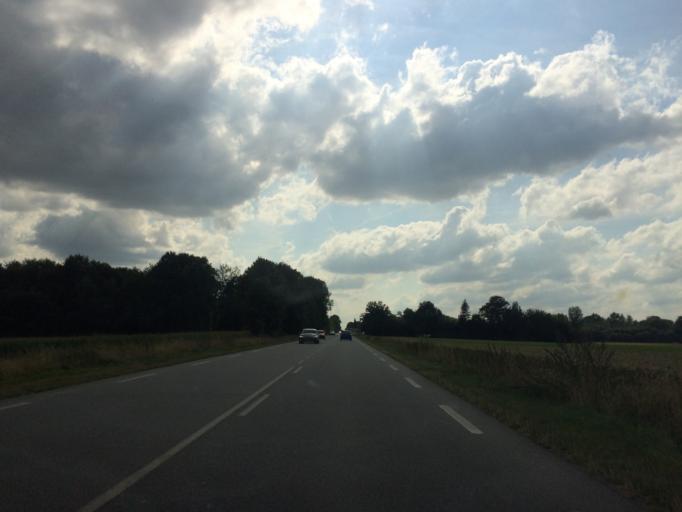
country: FR
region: Lower Normandy
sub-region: Departement de l'Orne
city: Tourouvre
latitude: 48.5620
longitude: 0.6121
